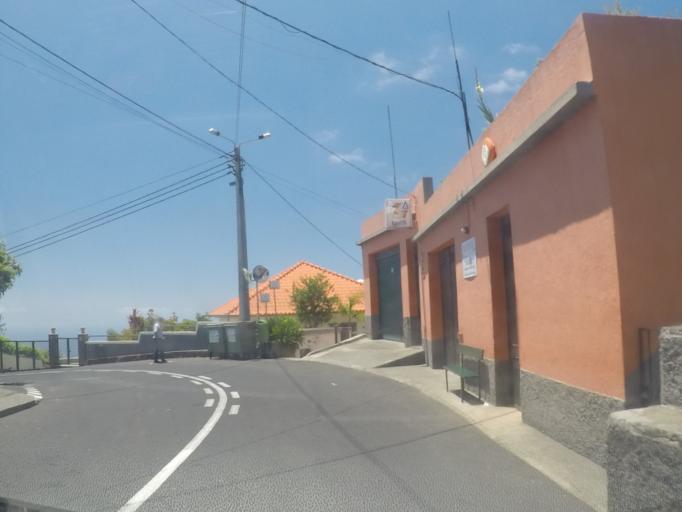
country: PT
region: Madeira
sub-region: Camara de Lobos
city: Curral das Freiras
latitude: 32.6810
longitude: -16.9909
